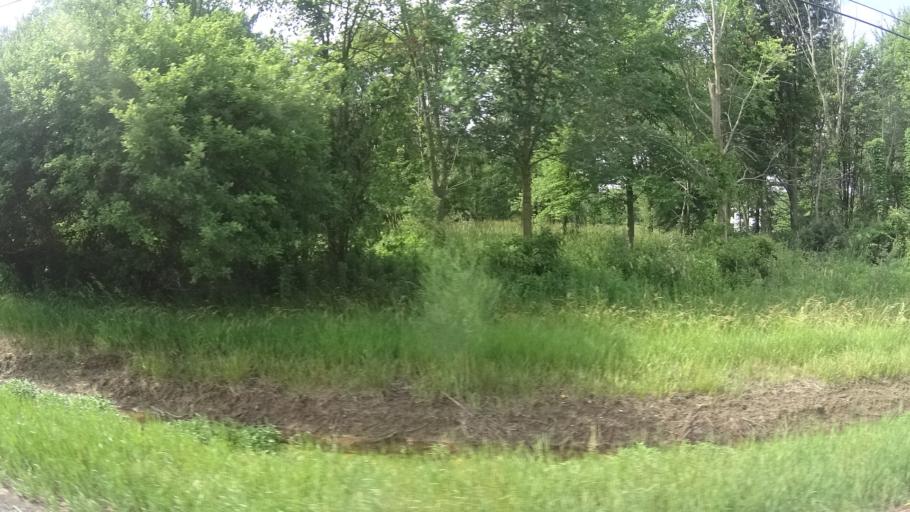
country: US
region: Ohio
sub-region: Erie County
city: Milan
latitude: 41.3041
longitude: -82.5036
